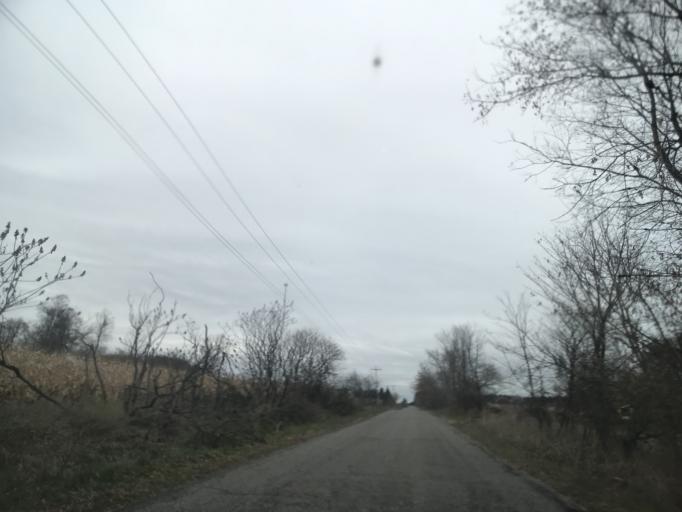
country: US
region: Wisconsin
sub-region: Menominee County
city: Legend Lake
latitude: 45.1732
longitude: -88.4556
